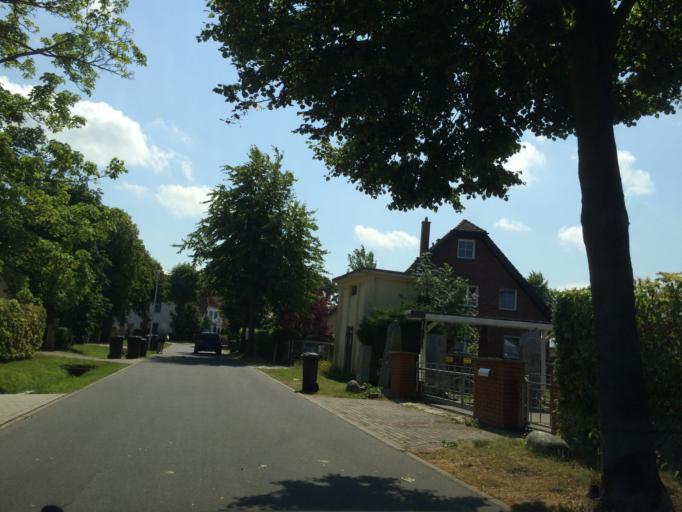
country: DE
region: Mecklenburg-Vorpommern
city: Zingst
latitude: 54.4340
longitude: 12.6806
